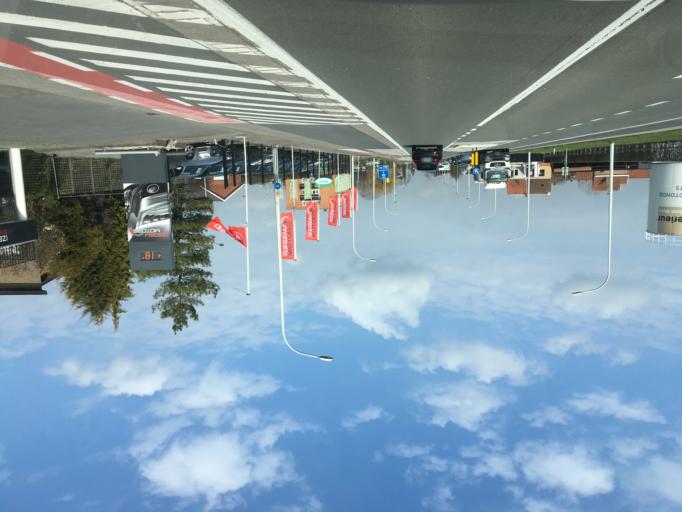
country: BE
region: Flanders
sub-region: Provincie West-Vlaanderen
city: Izegem
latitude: 50.9080
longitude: 3.2112
